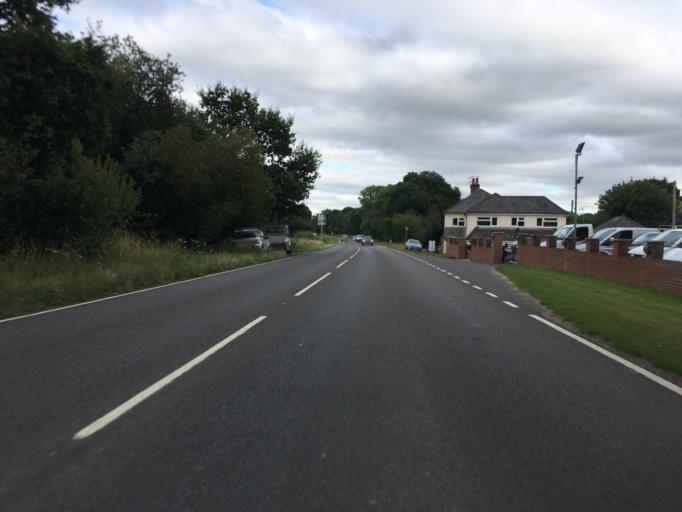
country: GB
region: England
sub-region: Hampshire
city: Liss
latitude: 51.0067
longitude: -0.8884
